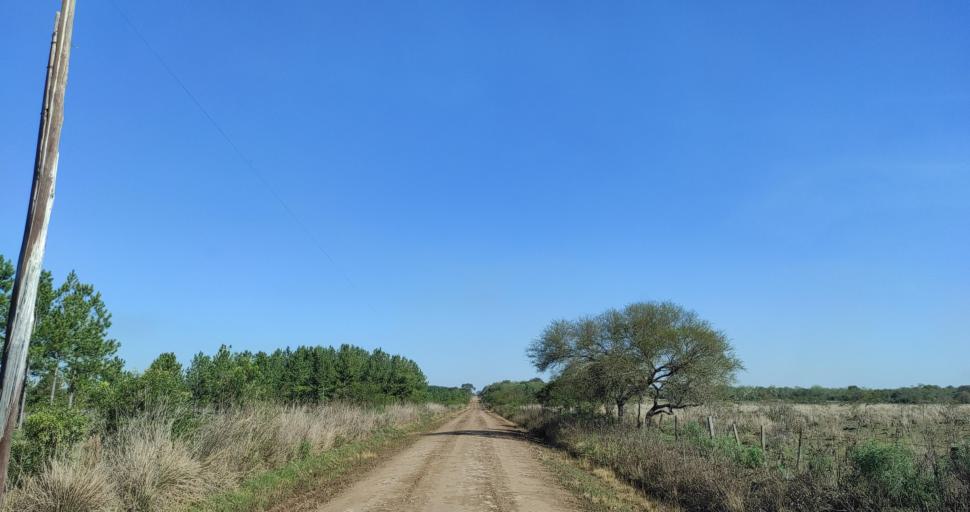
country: AR
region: Misiones
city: Cerro Cora
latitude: -27.6429
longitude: -55.6567
